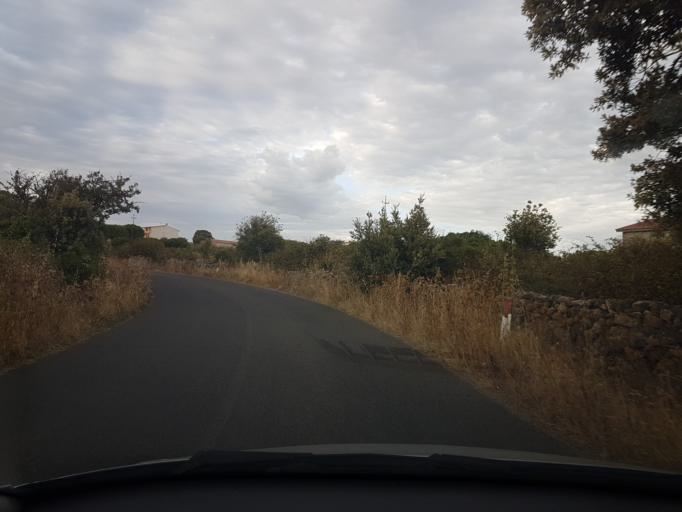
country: IT
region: Sardinia
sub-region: Provincia di Oristano
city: Seneghe
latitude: 40.0770
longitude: 8.6067
